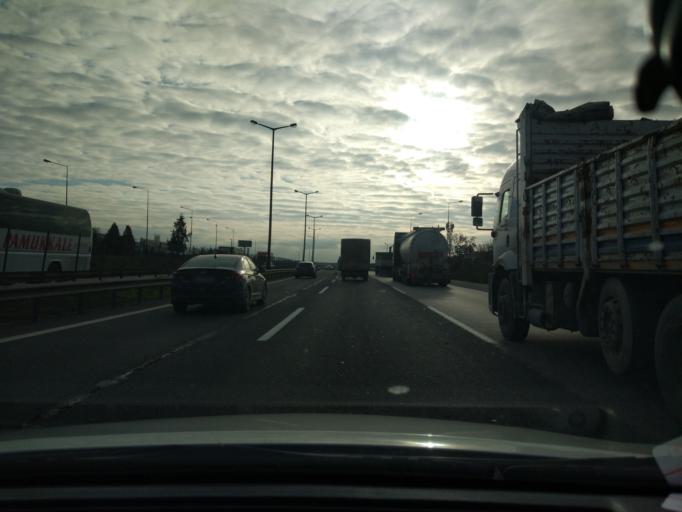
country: TR
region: Kocaeli
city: Gebze
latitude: 40.8357
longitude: 29.4211
